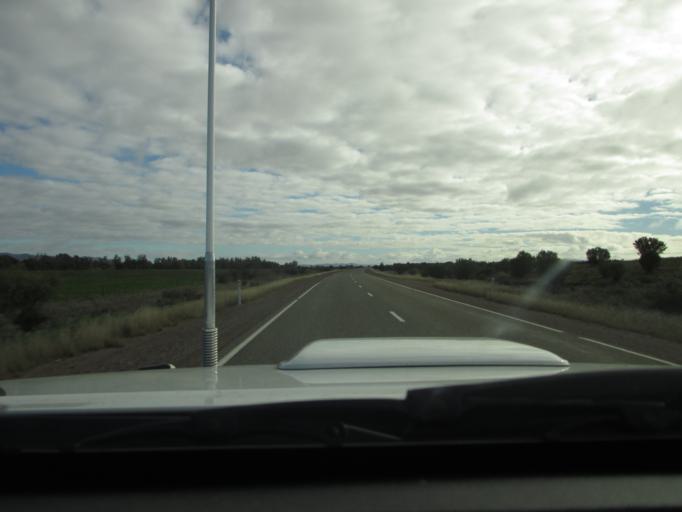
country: AU
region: South Australia
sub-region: Flinders Ranges
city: Quorn
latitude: -32.4737
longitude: 138.5406
